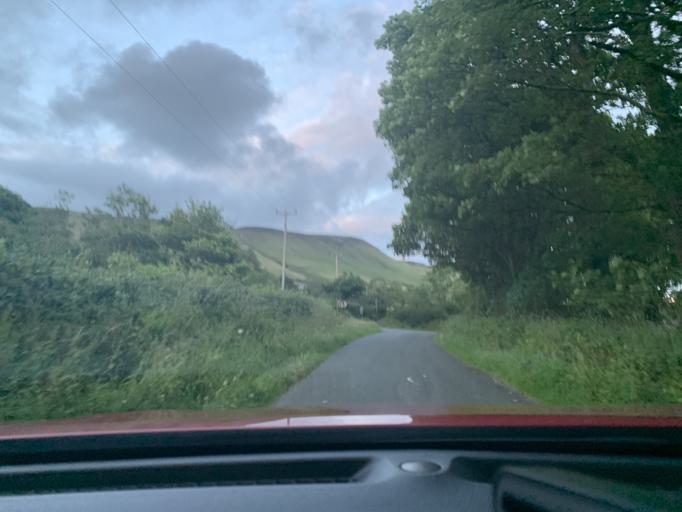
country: IE
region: Connaught
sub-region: Sligo
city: Sligo
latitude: 54.3531
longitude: -8.4886
